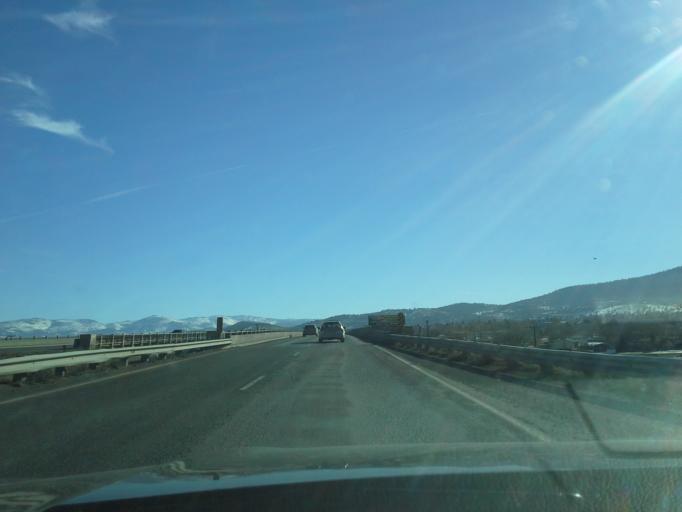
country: US
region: Montana
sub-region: Lewis and Clark County
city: Helena
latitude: 46.5999
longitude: -112.0042
